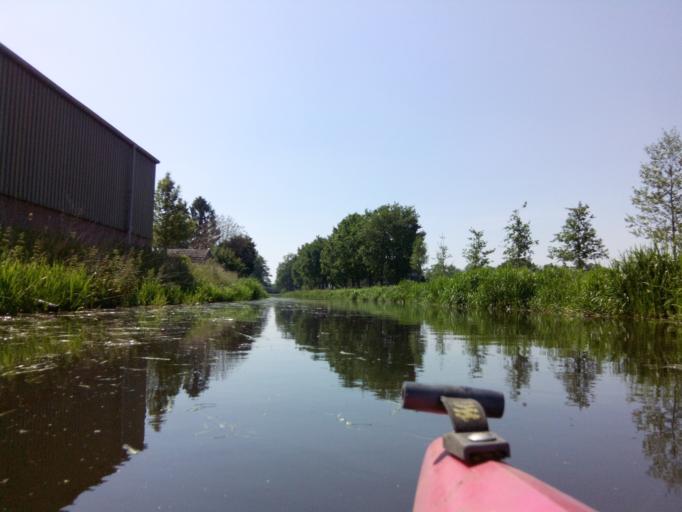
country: NL
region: Utrecht
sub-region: Gemeente Amersfoort
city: Randenbroek
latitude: 52.1171
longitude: 5.4008
